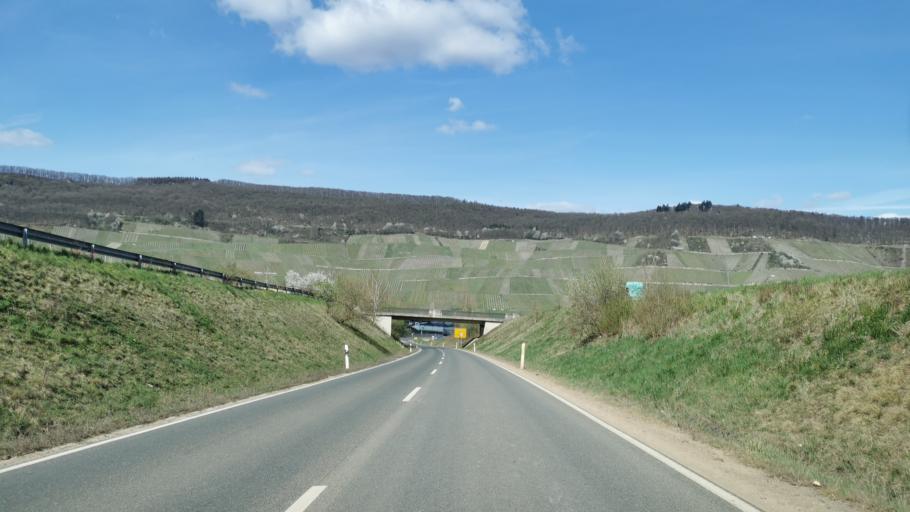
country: DE
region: Rheinland-Pfalz
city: Piesport
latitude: 49.8781
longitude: 6.9196
